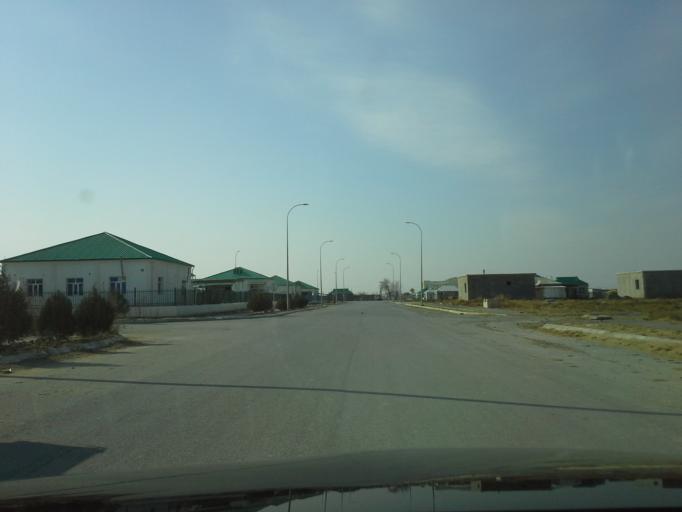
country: TM
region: Ahal
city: Abadan
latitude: 38.1745
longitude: 58.0509
